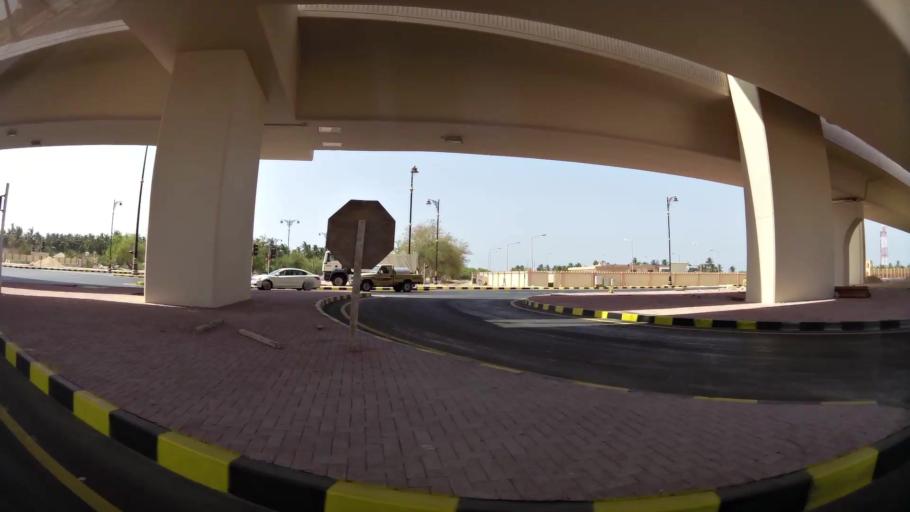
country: OM
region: Zufar
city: Salalah
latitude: 17.0322
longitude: 54.1421
